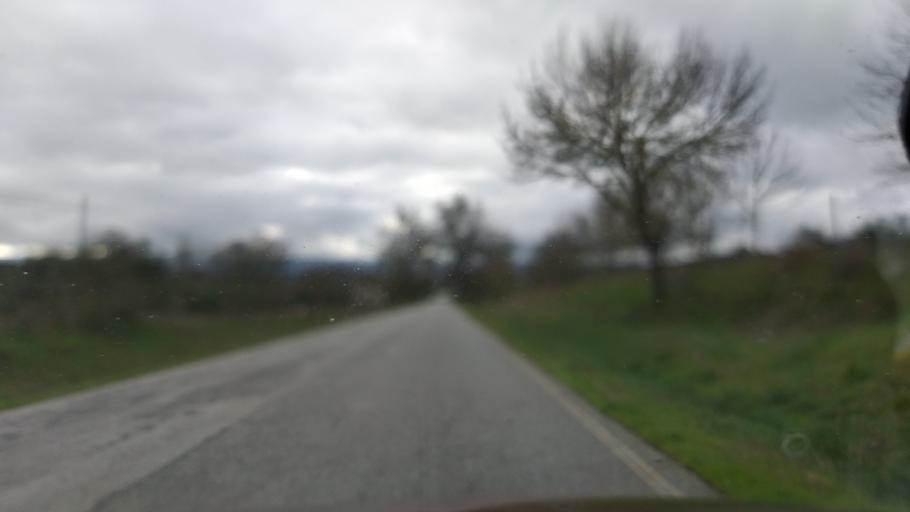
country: PT
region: Guarda
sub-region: Celorico da Beira
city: Celorico da Beira
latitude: 40.6938
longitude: -7.3707
